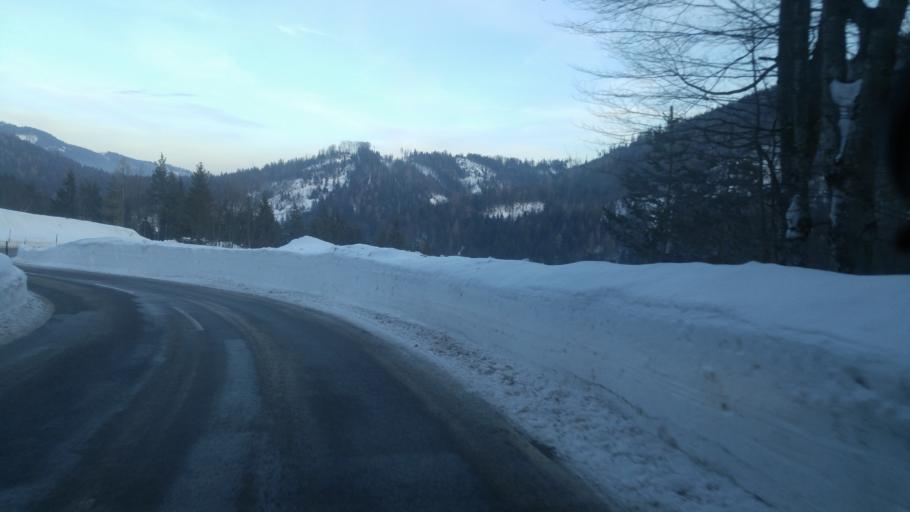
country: AT
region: Lower Austria
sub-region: Politischer Bezirk Lilienfeld
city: Hohenberg
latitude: 47.8868
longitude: 15.6615
